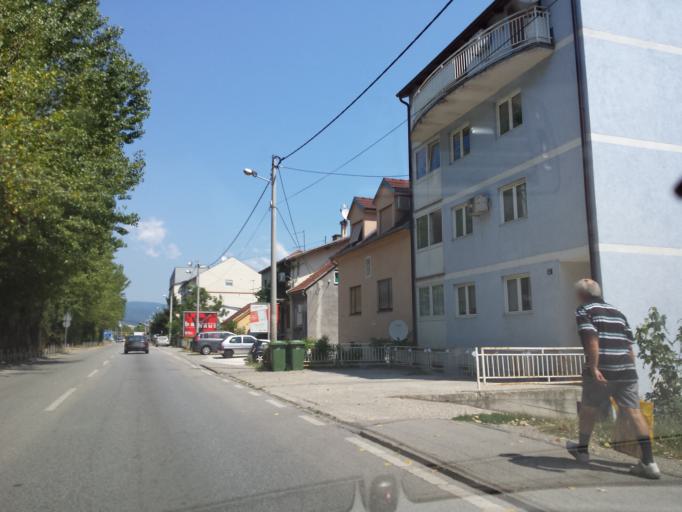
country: HR
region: Grad Zagreb
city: Zagreb
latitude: 45.8074
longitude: 16.0143
